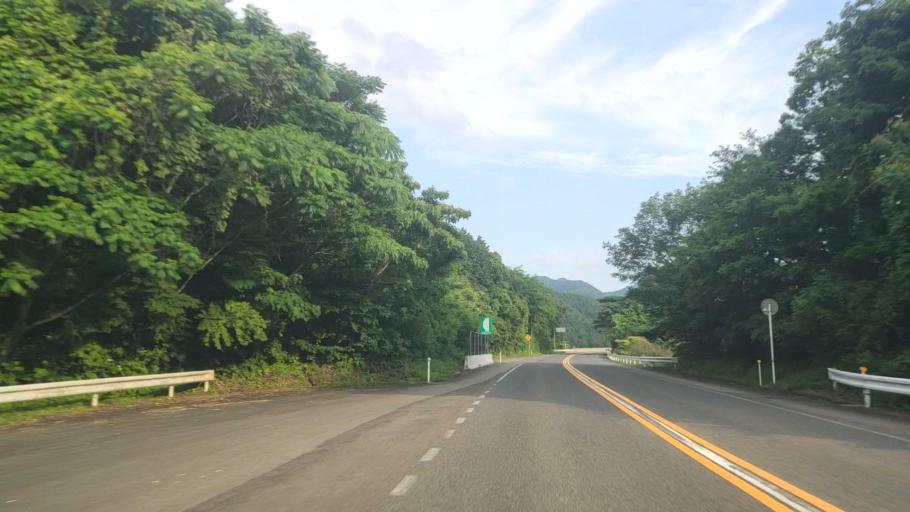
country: JP
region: Tottori
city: Kurayoshi
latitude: 35.3355
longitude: 133.7545
